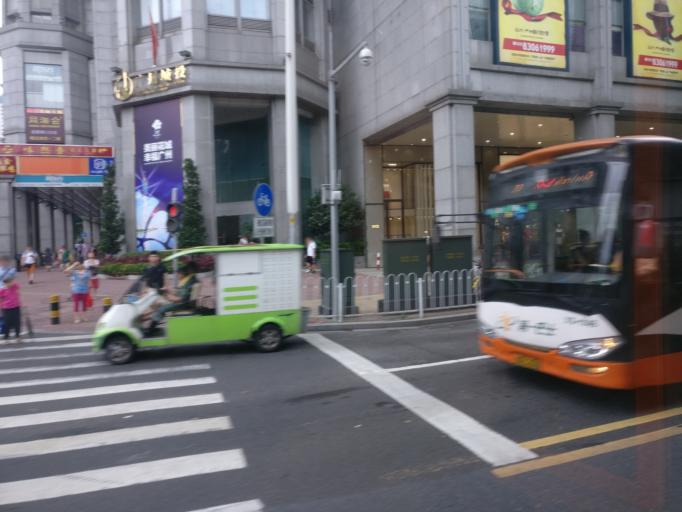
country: CN
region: Guangdong
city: Guangzhou
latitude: 23.1289
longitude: 113.2677
